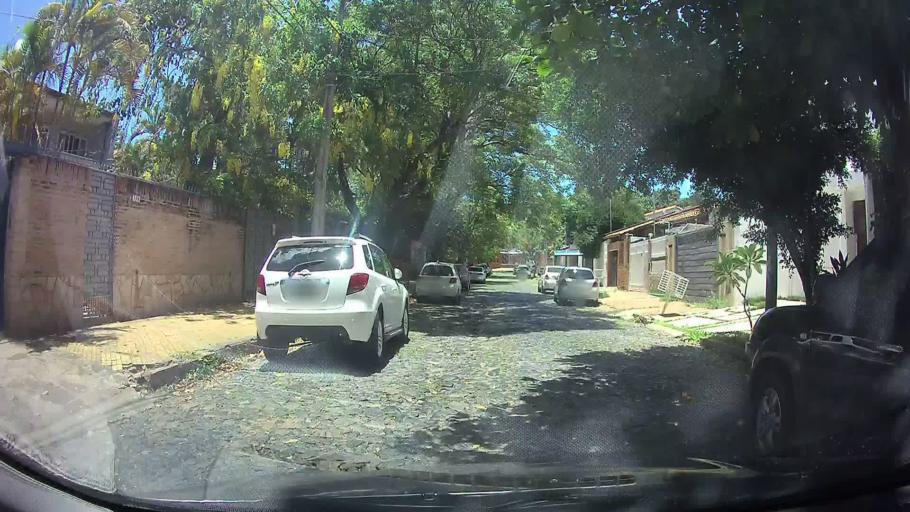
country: PY
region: Asuncion
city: Asuncion
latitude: -25.2899
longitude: -57.6075
